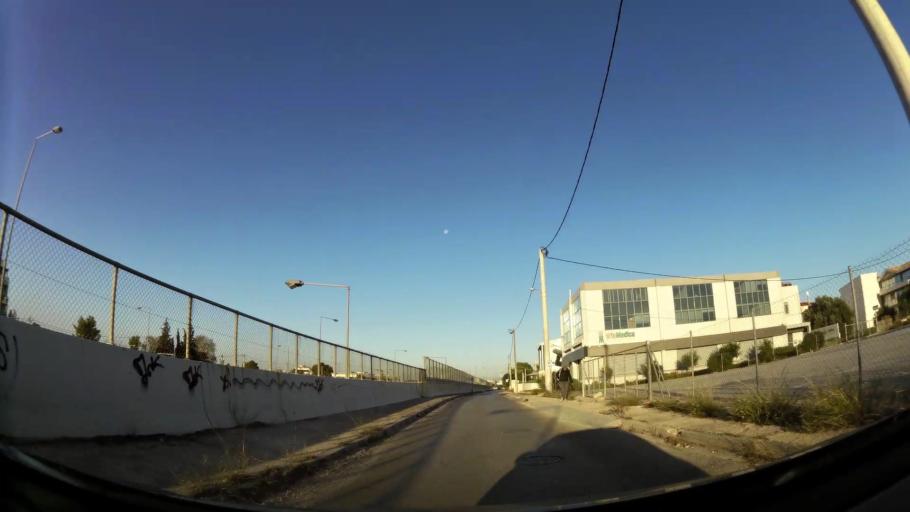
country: GR
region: Attica
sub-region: Nomarchia Athinas
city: Agia Paraskevi
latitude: 38.0234
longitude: 23.8403
